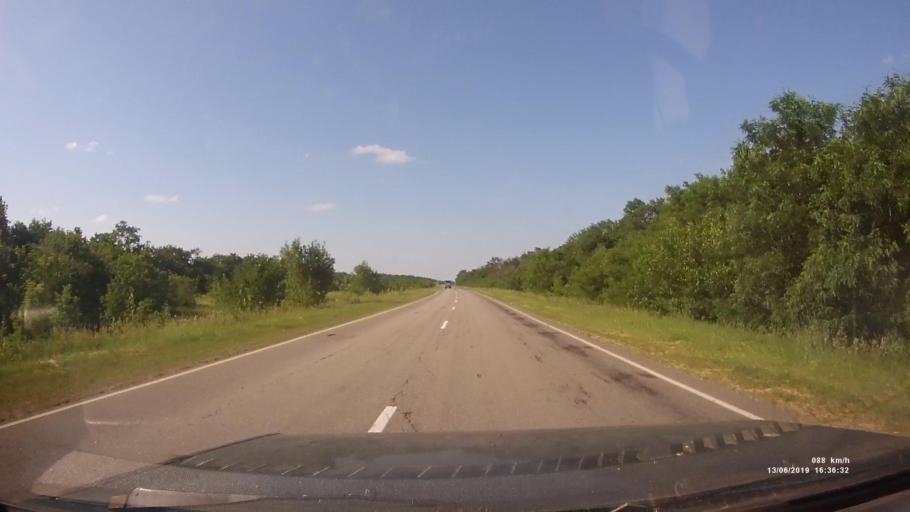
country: RU
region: Rostov
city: Kazanskaya
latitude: 49.8962
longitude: 41.3066
